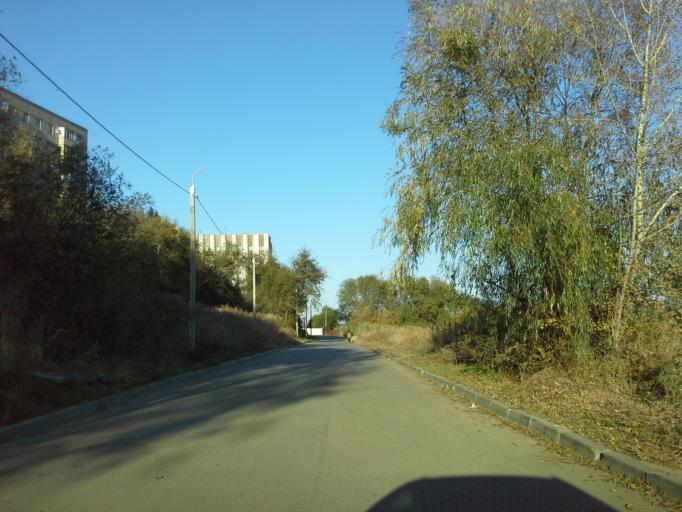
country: RU
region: Volgograd
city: Vodstroy
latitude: 48.8208
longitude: 44.6424
